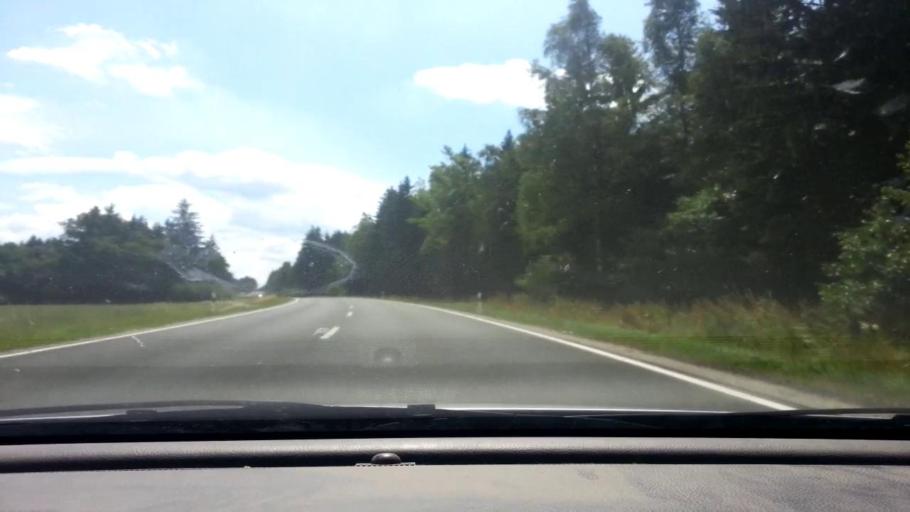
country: DE
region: Bavaria
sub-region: Upper Palatinate
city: Erbendorf
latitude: 49.8460
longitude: 11.9987
